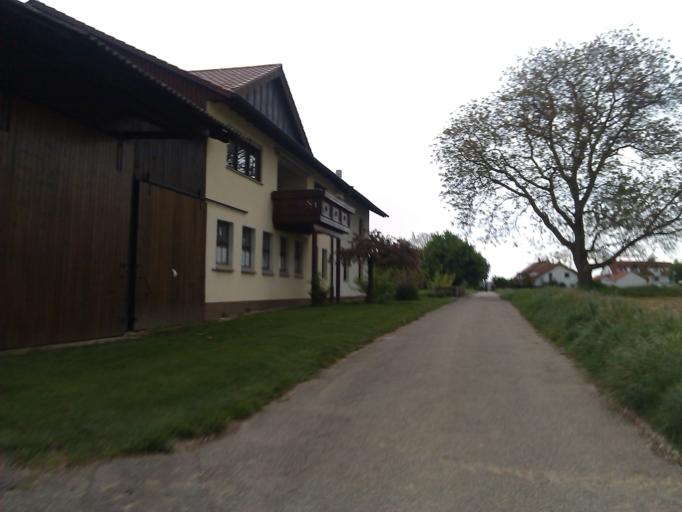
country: DE
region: Baden-Wuerttemberg
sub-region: Regierungsbezirk Stuttgart
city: Neckarsulm
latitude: 49.1732
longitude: 9.1922
